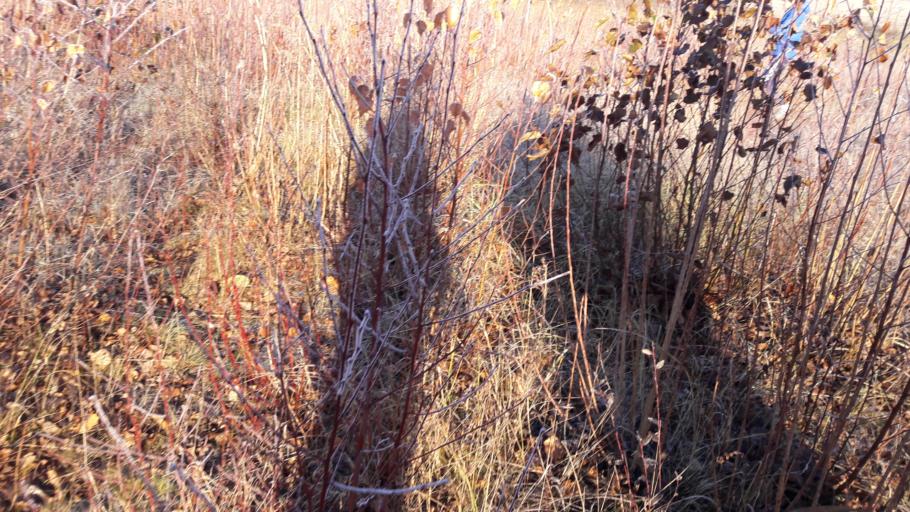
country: NL
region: Flevoland
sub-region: Gemeente Almere
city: Almere Stad
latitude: 52.3758
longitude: 5.2280
